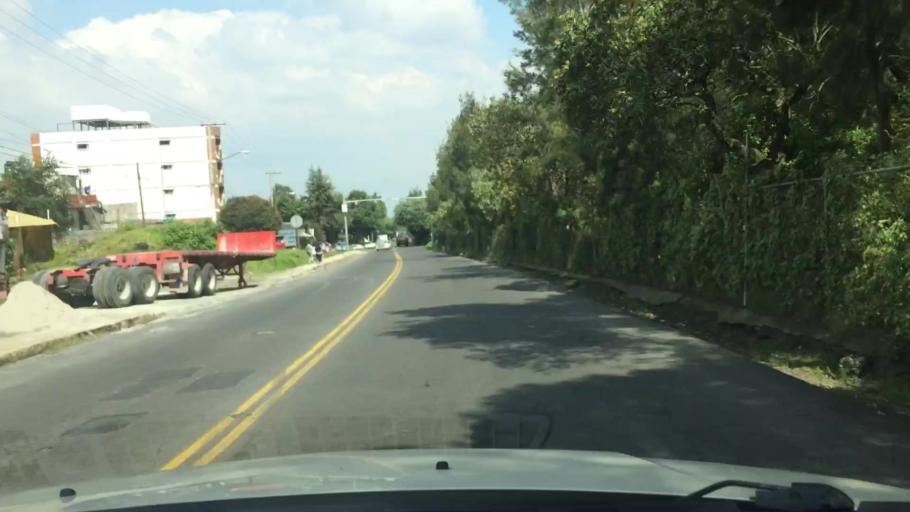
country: MX
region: Mexico City
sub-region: Tlalpan
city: Lomas de Tepemecatl
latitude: 19.2682
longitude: -99.2188
